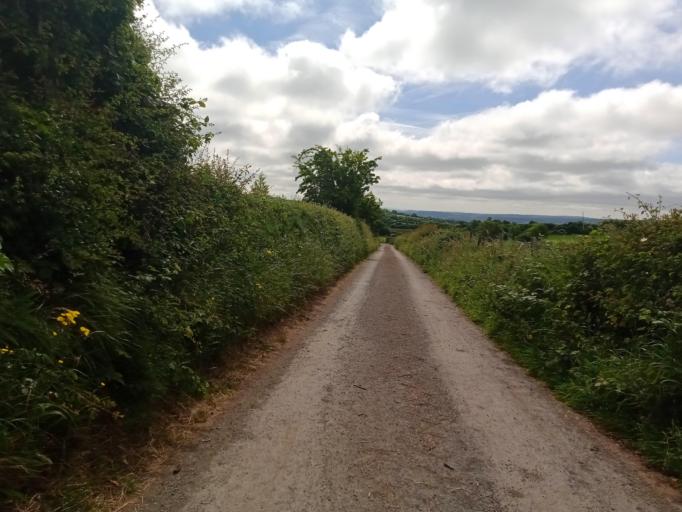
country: IE
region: Leinster
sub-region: Kilkenny
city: Ballyragget
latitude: 52.7831
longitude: -7.4562
